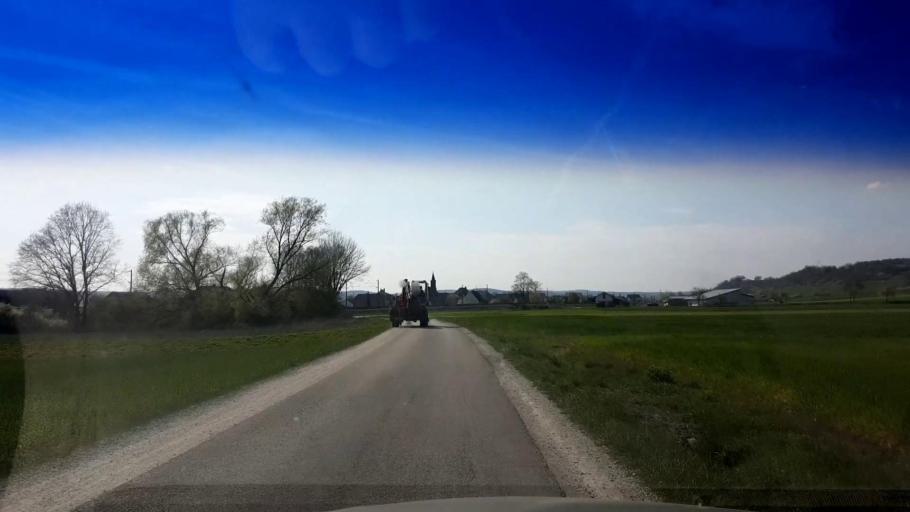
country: DE
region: Bavaria
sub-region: Upper Franconia
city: Oberhaid
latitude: 49.9356
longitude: 10.7981
